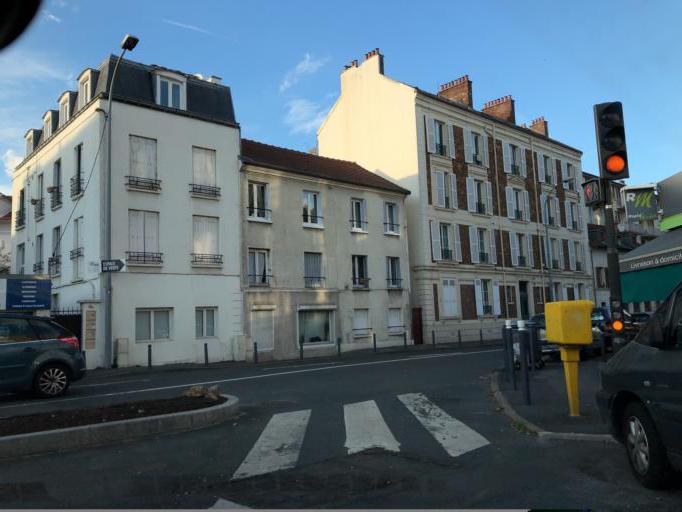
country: FR
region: Ile-de-France
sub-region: Departement des Hauts-de-Seine
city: Chaville
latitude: 48.8006
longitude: 2.1872
